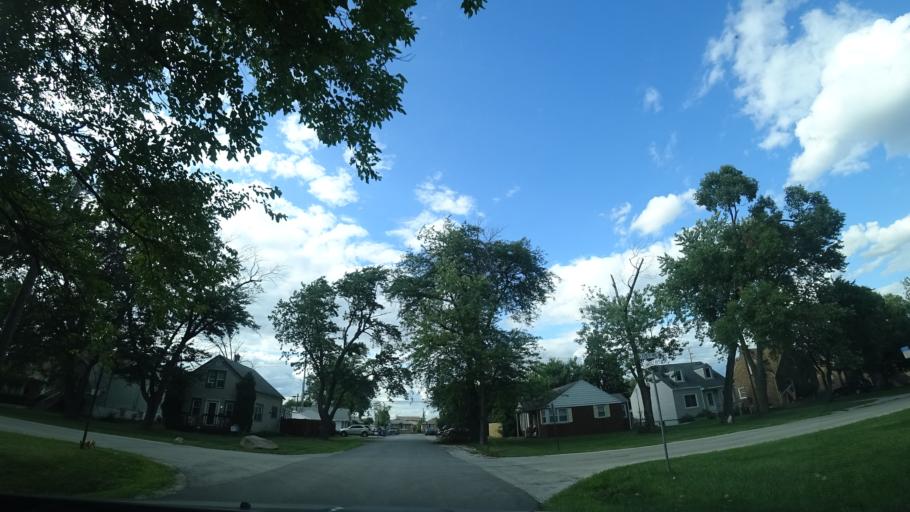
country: US
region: Illinois
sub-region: Cook County
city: Merrionette Park
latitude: 41.6829
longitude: -87.7127
